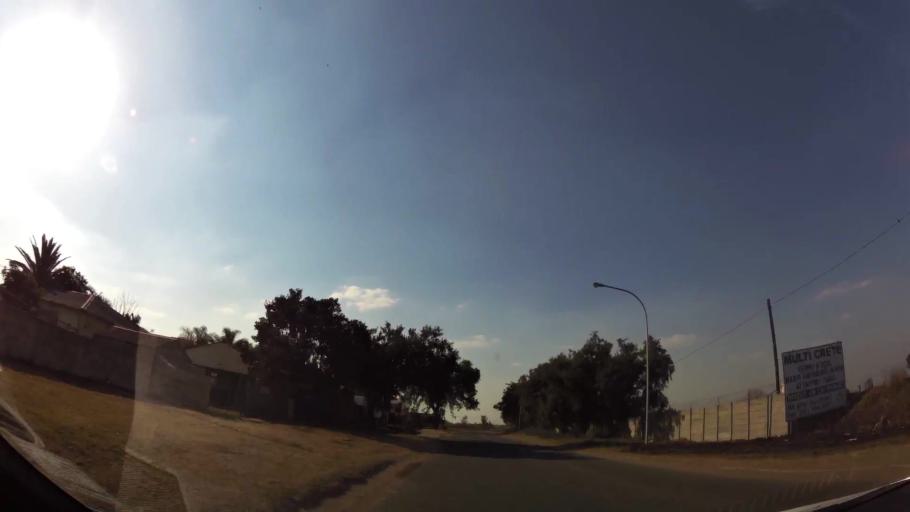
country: ZA
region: Gauteng
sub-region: Ekurhuleni Metropolitan Municipality
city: Brakpan
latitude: -26.2204
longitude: 28.3624
